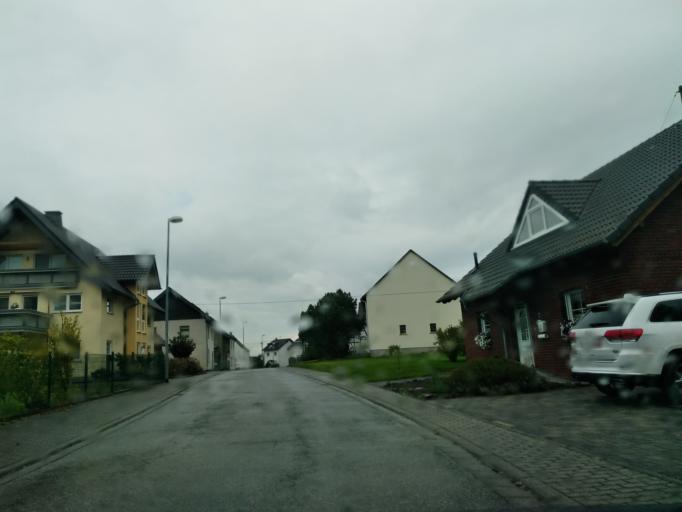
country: DE
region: Rheinland-Pfalz
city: Kircheib
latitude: 50.6840
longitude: 7.4480
